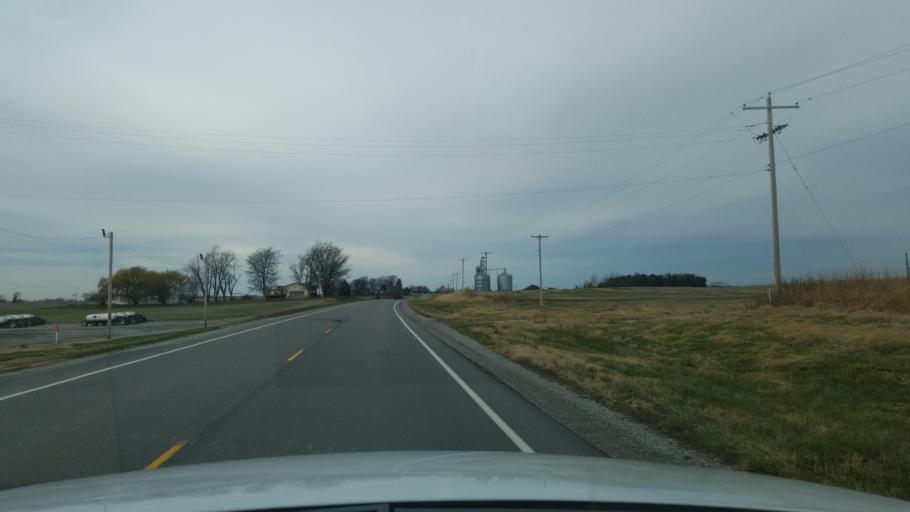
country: US
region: Illinois
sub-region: White County
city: Carmi
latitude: 37.9078
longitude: -88.1435
